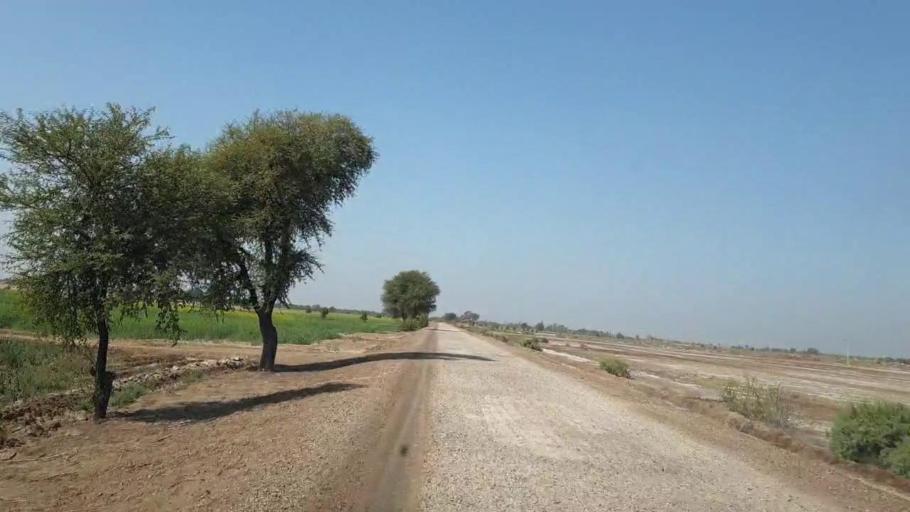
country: PK
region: Sindh
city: Mirpur Khas
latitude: 25.6947
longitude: 69.1070
